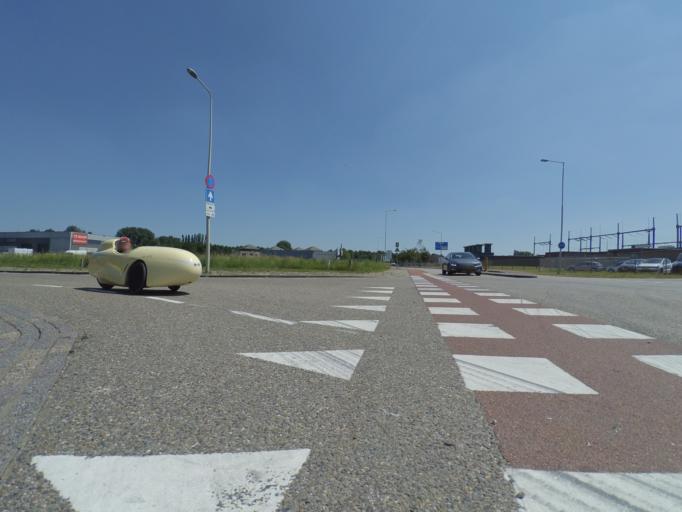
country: NL
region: North Brabant
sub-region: Gemeente Bergen op Zoom
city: Halsteren
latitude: 51.5061
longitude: 4.2705
